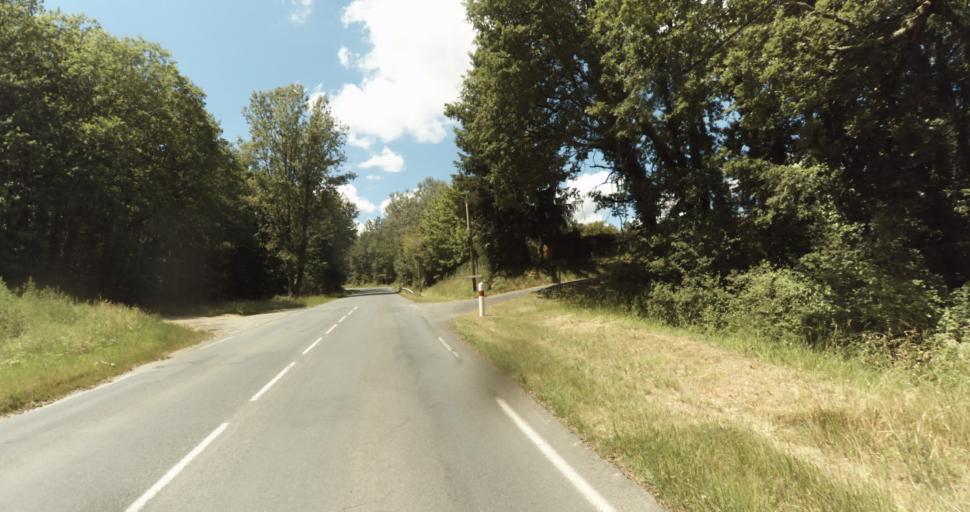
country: FR
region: Aquitaine
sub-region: Departement de la Dordogne
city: Le Bugue
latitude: 44.8425
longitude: 0.8836
